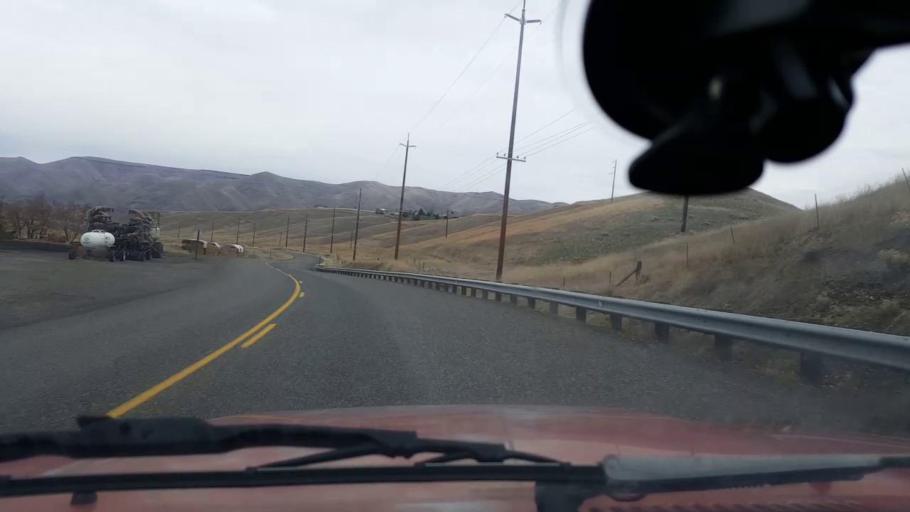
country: US
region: Washington
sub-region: Asotin County
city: Clarkston Heights-Vineland
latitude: 46.4002
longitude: -117.1009
